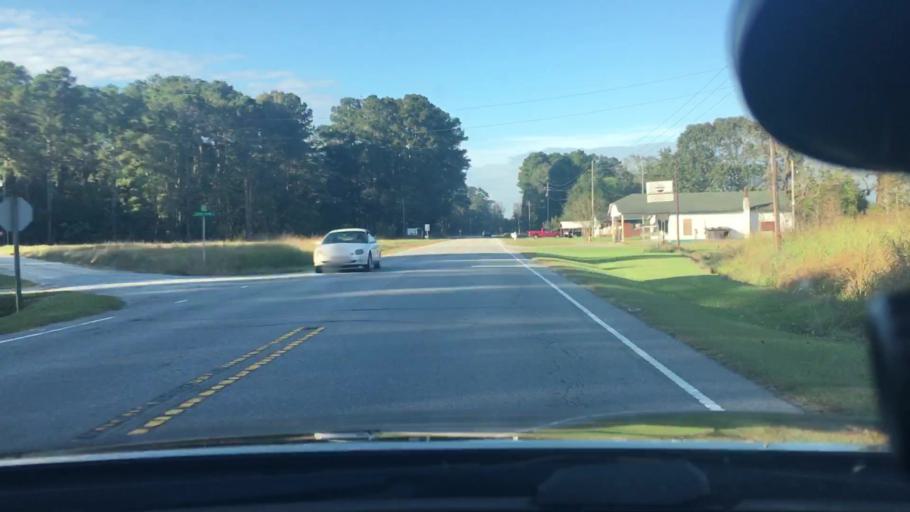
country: US
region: North Carolina
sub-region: Pitt County
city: Windsor
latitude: 35.4480
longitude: -77.2636
